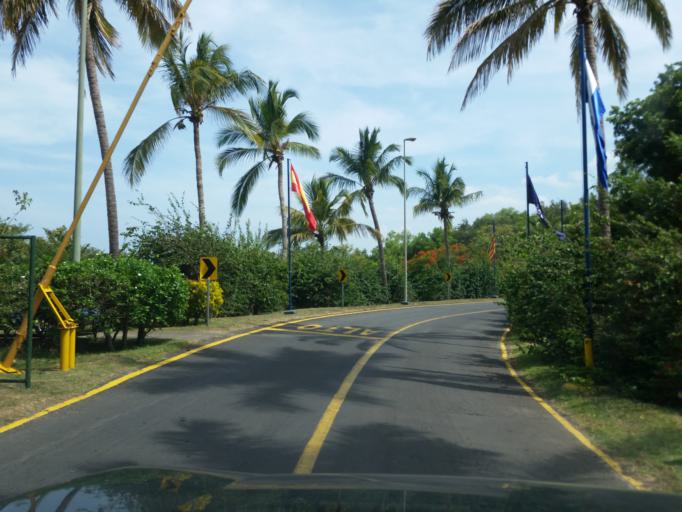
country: NI
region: Managua
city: Masachapa
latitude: 11.7997
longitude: -86.5190
